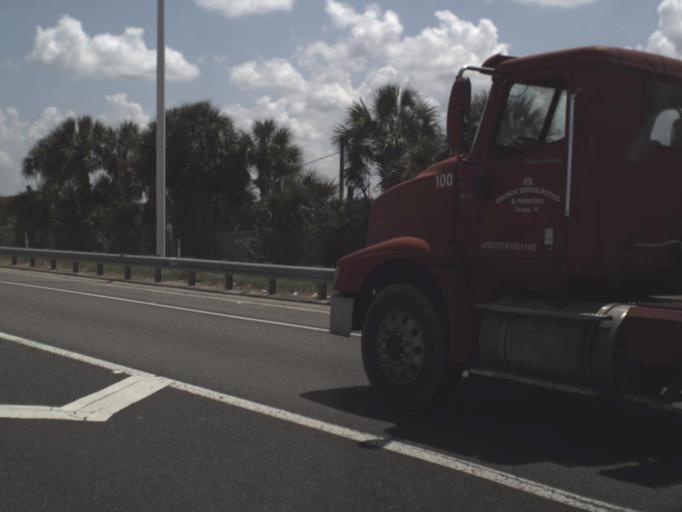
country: US
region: Florida
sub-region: Hillsborough County
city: East Lake-Orient Park
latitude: 27.9723
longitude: -82.3958
